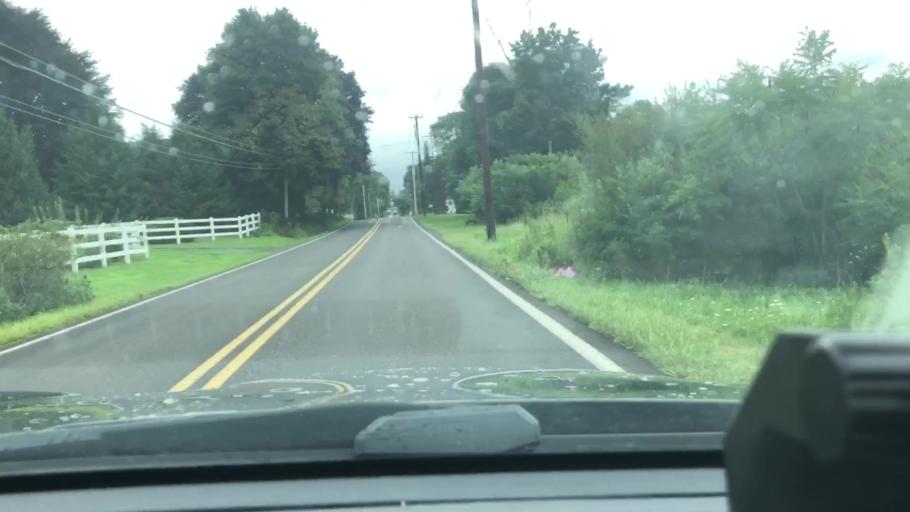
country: US
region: Pennsylvania
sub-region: Lehigh County
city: Coopersburg
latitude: 40.4928
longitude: -75.3948
